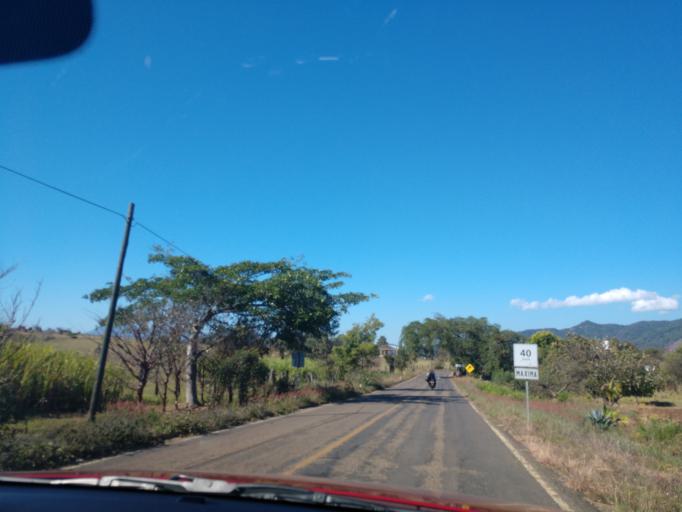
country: MX
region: Nayarit
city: Compostela
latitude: 21.2688
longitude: -104.8919
